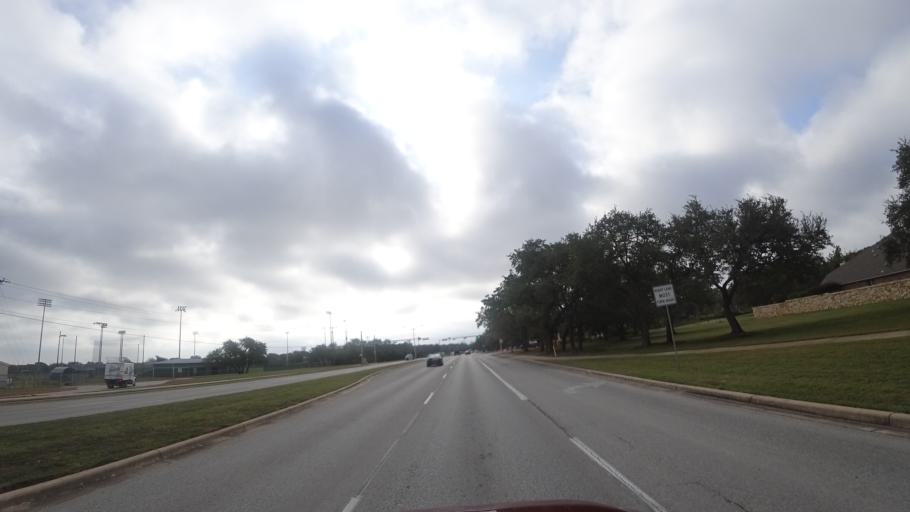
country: US
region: Texas
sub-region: Williamson County
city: Anderson Mill
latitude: 30.4702
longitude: -97.8457
